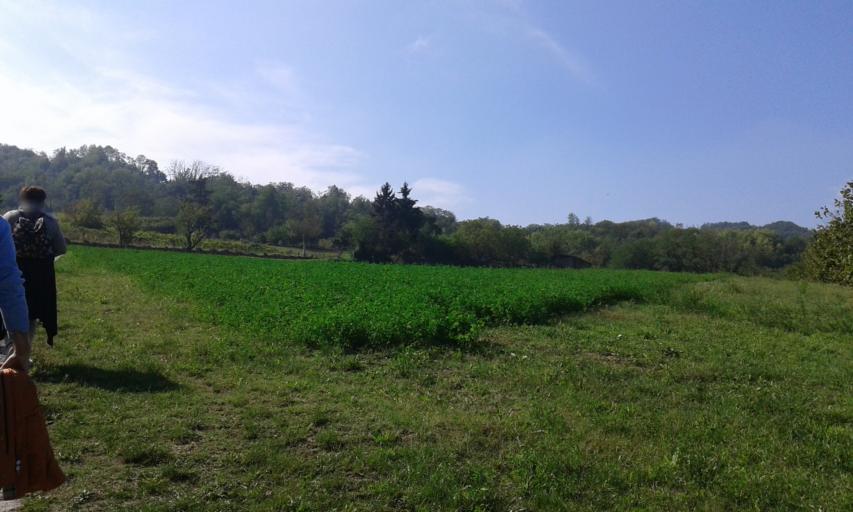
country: IT
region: Piedmont
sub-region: Provincia di Asti
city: Monastero Bormida
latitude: 44.6431
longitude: 8.3319
